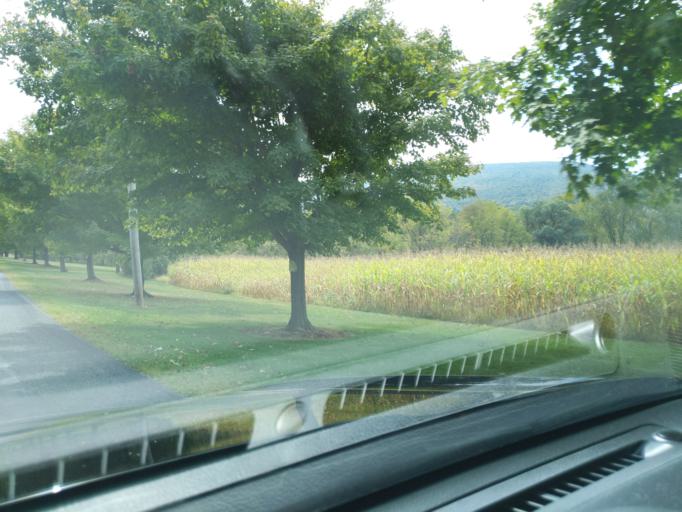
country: US
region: Pennsylvania
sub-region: Blair County
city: Hollidaysburg
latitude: 40.4265
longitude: -78.3483
